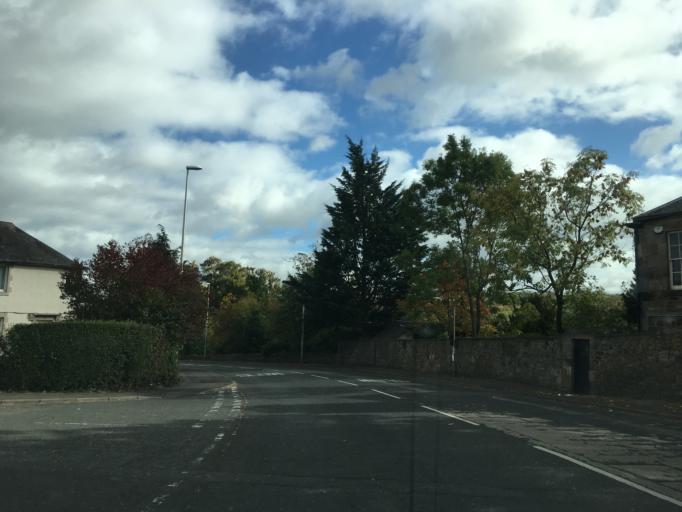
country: GB
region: Scotland
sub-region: Midlothian
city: Dalkeith
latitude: 55.8922
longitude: -3.0667
